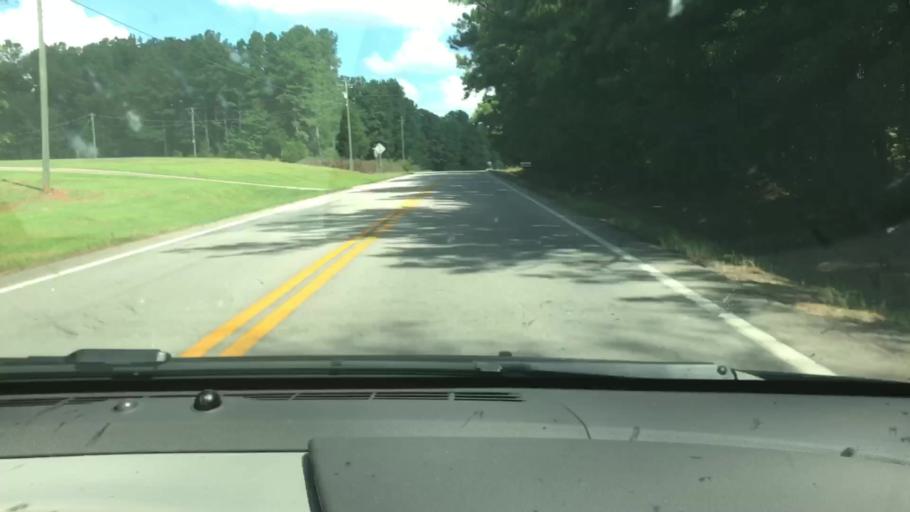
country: US
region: Georgia
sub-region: Troup County
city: La Grange
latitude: 32.9442
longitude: -85.0182
